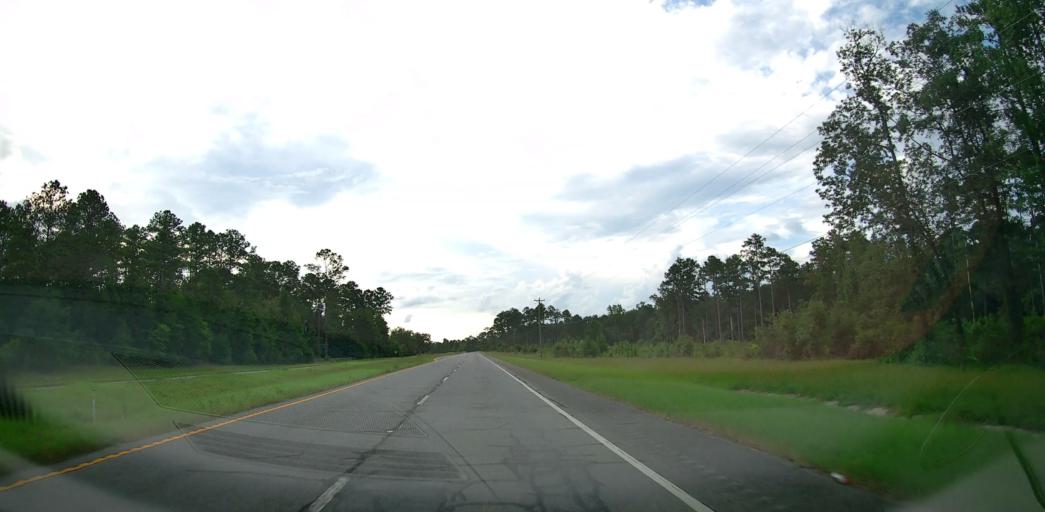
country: US
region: Georgia
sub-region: Pulaski County
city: Hawkinsville
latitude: 32.2642
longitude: -83.4096
